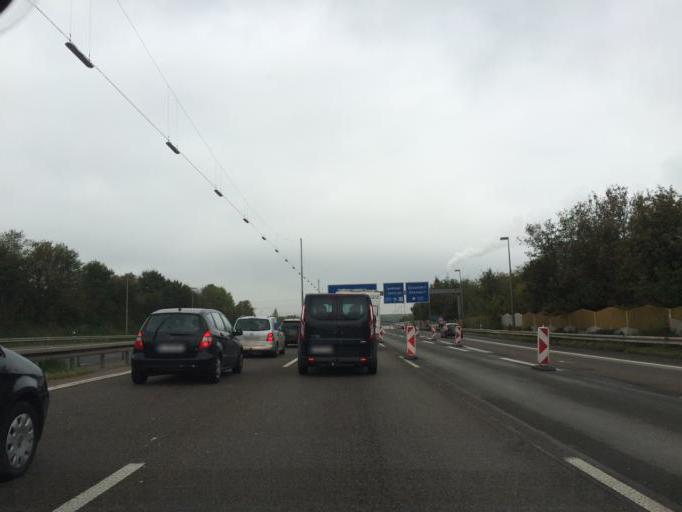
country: DE
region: North Rhine-Westphalia
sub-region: Regierungsbezirk Koln
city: Leverkusen
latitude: 51.0380
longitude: 6.9832
